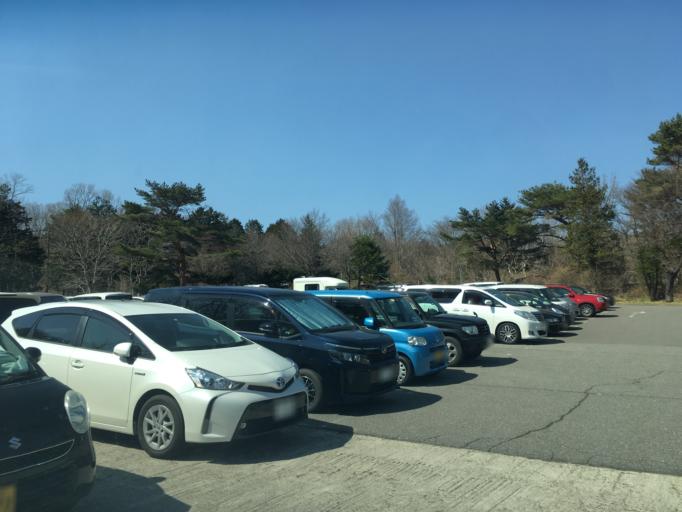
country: JP
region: Tochigi
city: Kuroiso
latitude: 37.0786
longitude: 140.0007
